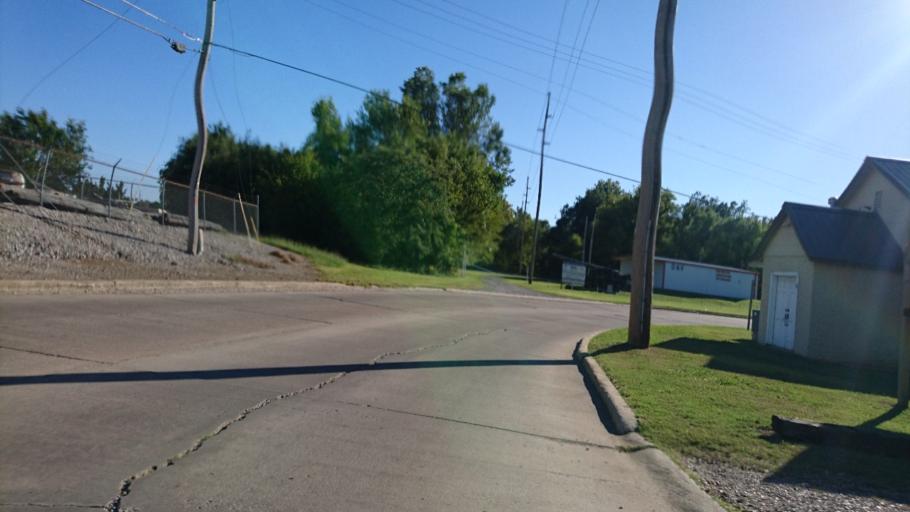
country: US
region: Oklahoma
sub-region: Rogers County
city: Claremore
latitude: 36.3113
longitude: -95.6201
